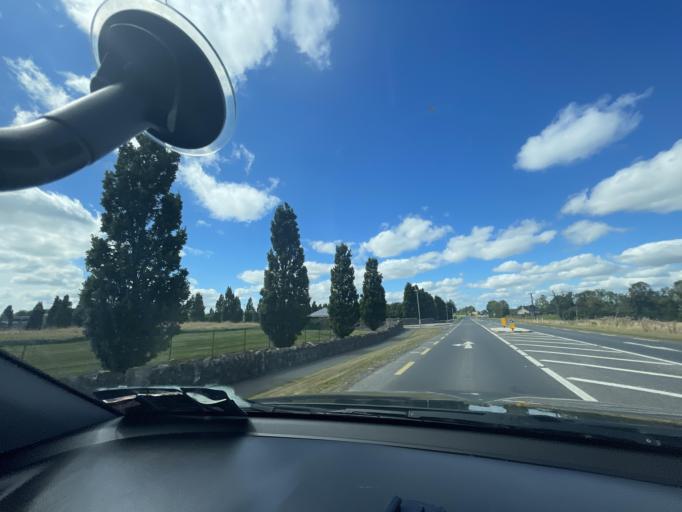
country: IE
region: Leinster
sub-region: An Mhi
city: Newtown Trim
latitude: 53.5242
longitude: -6.6629
